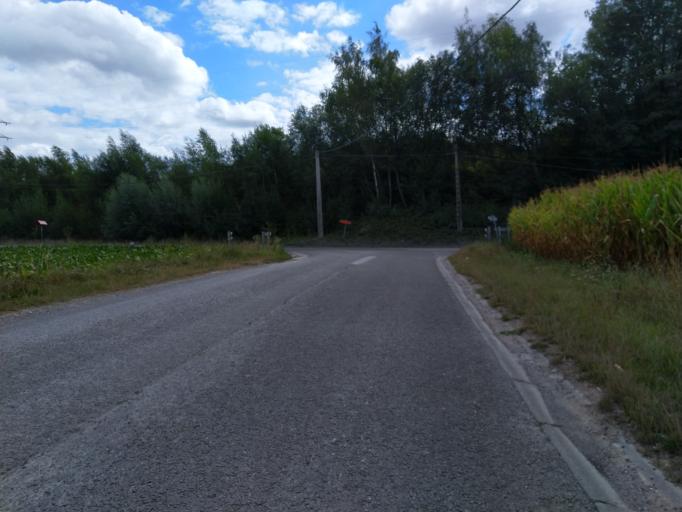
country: BE
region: Wallonia
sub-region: Province du Hainaut
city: Courcelles
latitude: 50.3960
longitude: 4.3612
